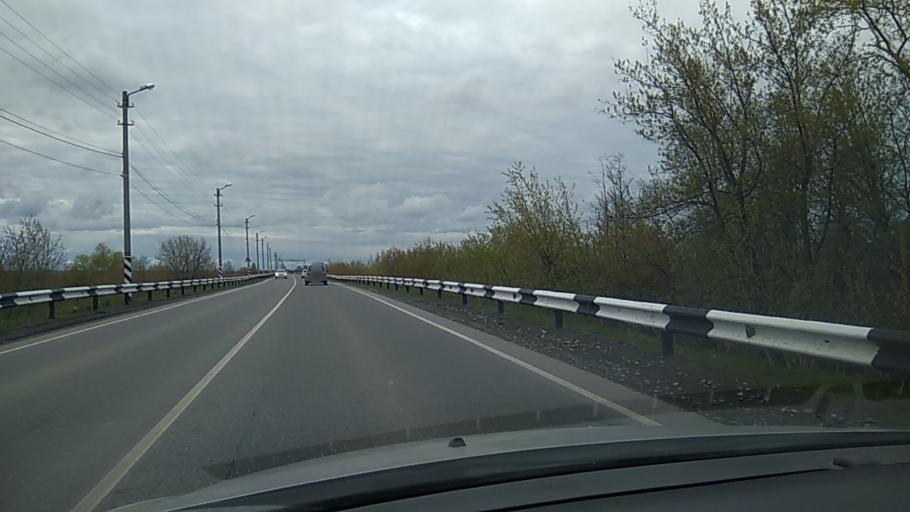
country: RU
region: Tjumen
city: Chervishevo
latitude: 56.9630
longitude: 65.4354
